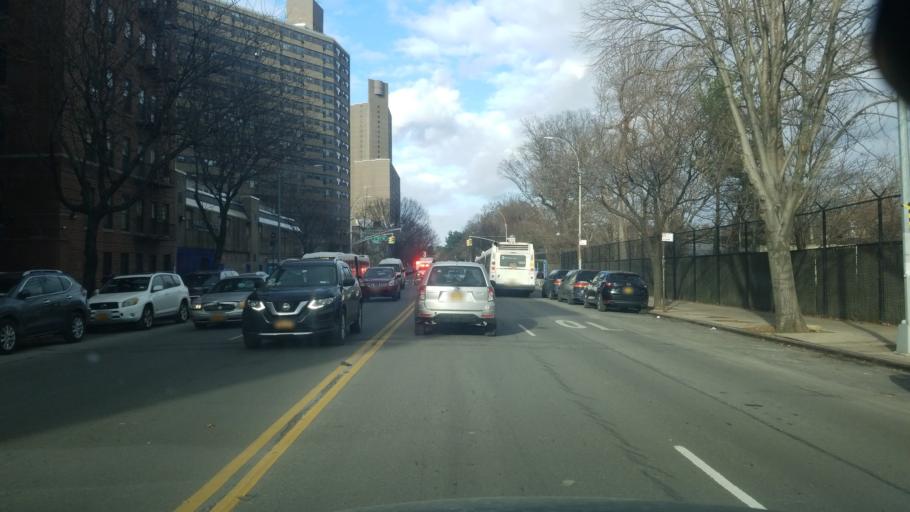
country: US
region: New York
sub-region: Bronx
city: The Bronx
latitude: 40.8526
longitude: -73.8819
